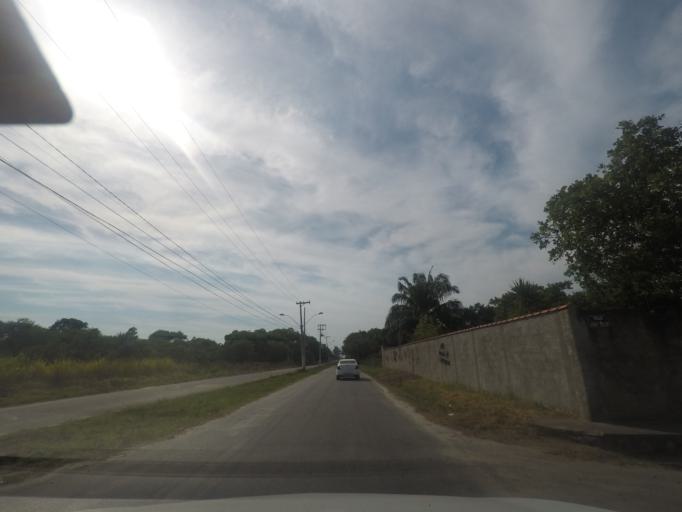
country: BR
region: Rio de Janeiro
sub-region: Marica
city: Marica
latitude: -22.9386
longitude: -42.8970
